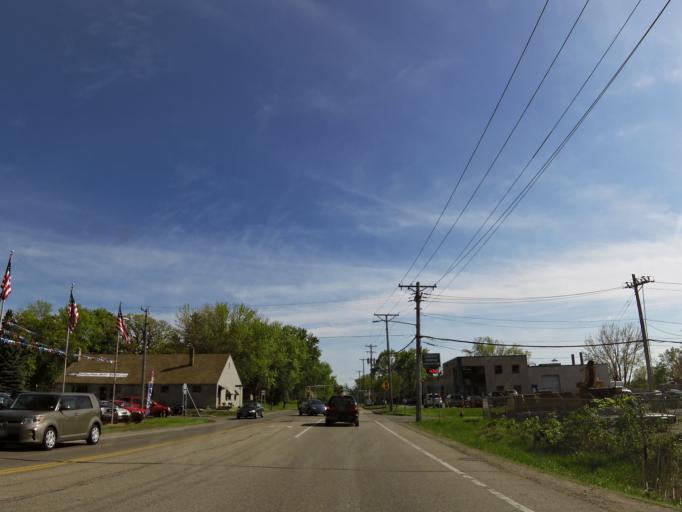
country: US
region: Minnesota
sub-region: Ramsey County
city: North Saint Paul
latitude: 45.0180
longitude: -92.9849
